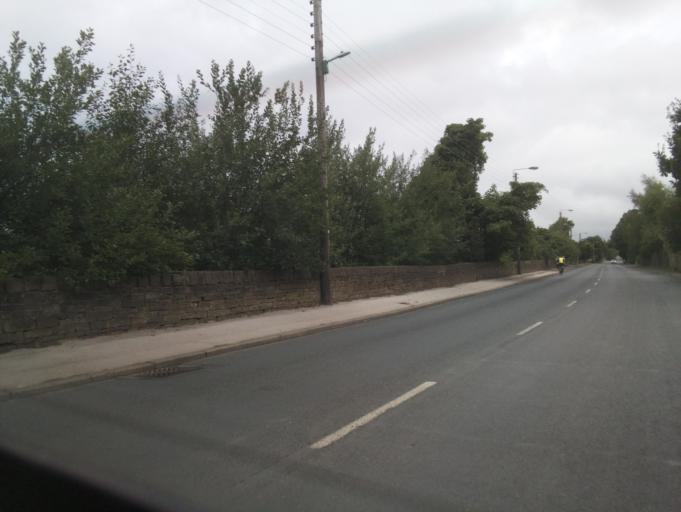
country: GB
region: England
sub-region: Kirklees
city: Holmfirth
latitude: 53.5758
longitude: -1.7803
